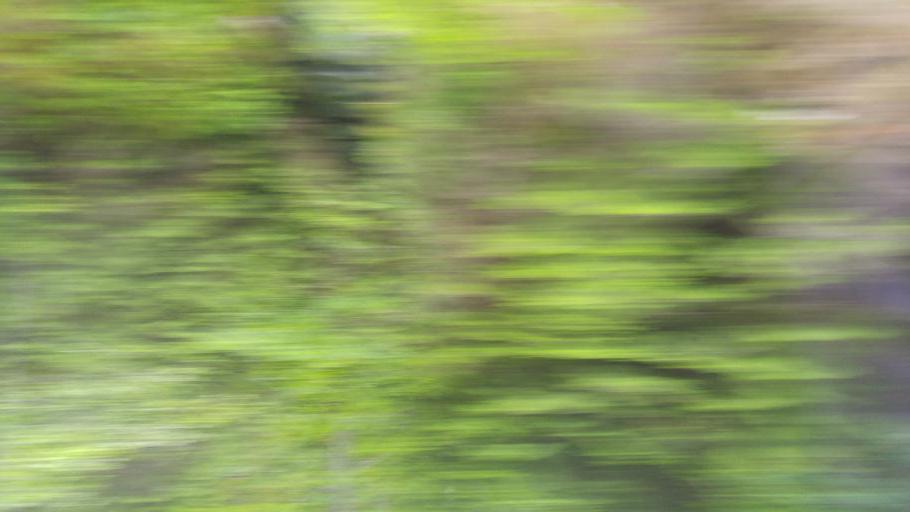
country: NO
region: Nord-Trondelag
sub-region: Meraker
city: Meraker
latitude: 63.4562
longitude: 11.5553
